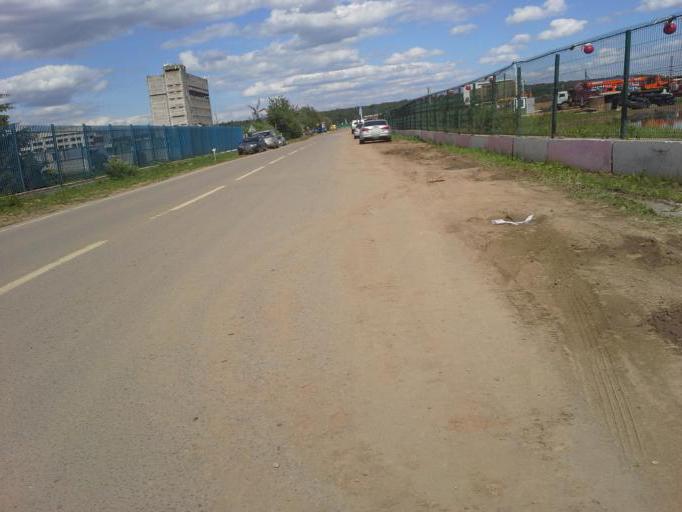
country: RU
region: Moskovskaya
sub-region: Leninskiy Rayon
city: Vnukovo
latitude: 55.6195
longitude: 37.2618
